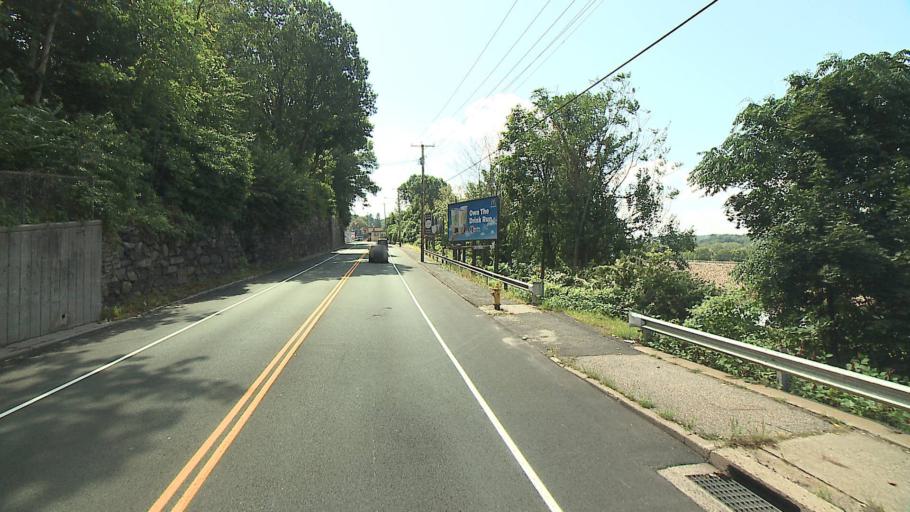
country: US
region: Connecticut
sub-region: New Haven County
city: Ansonia
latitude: 41.3343
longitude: -73.0763
